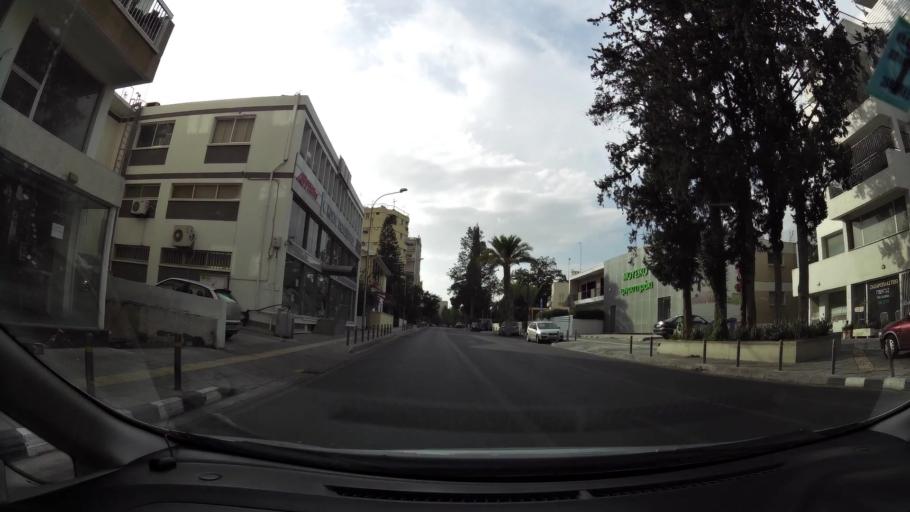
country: CY
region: Lefkosia
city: Nicosia
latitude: 35.1670
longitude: 33.3486
